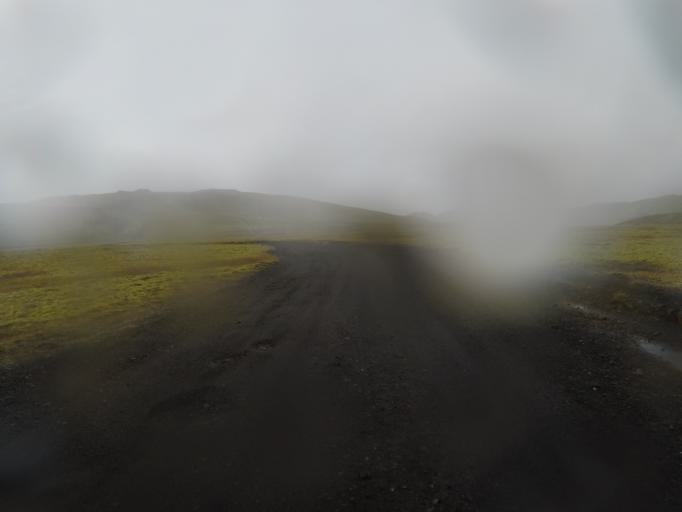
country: IS
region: South
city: Vestmannaeyjar
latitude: 63.9742
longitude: -18.8379
